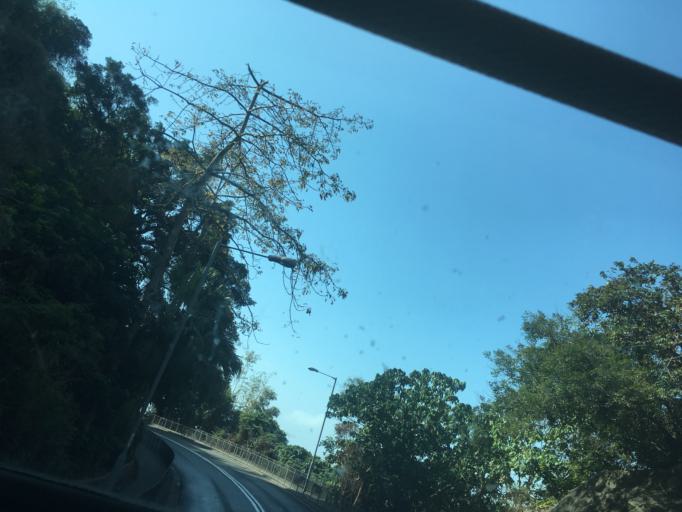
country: HK
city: Hong Kong
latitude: 22.2777
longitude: 114.1175
